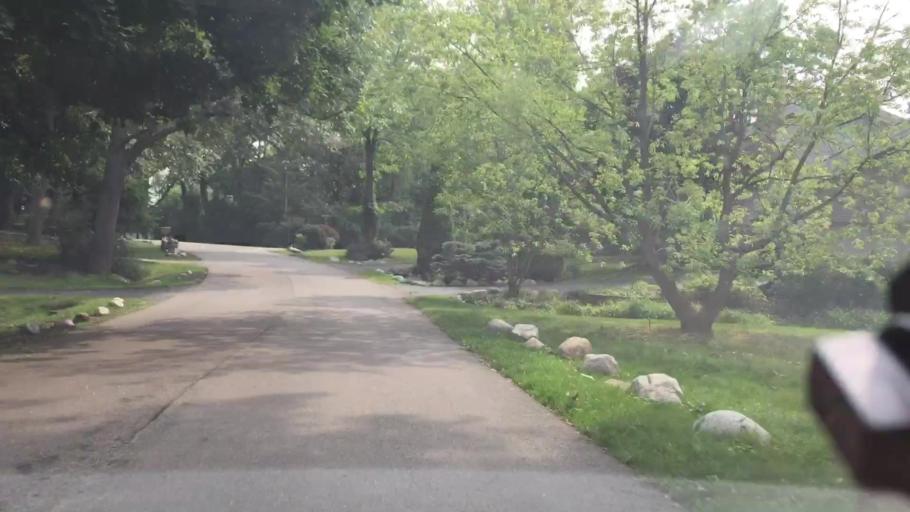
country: US
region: Michigan
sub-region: Oakland County
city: Sylvan Lake
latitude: 42.5972
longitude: -83.2915
